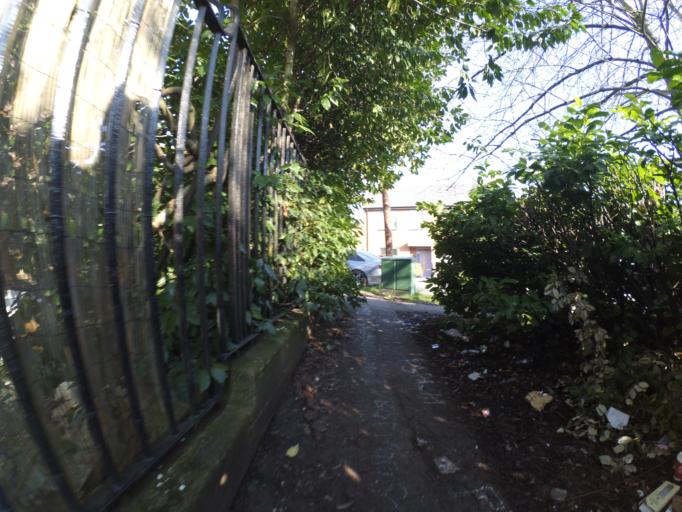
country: GB
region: England
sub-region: Greater London
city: Wembley
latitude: 51.5680
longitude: -0.2586
